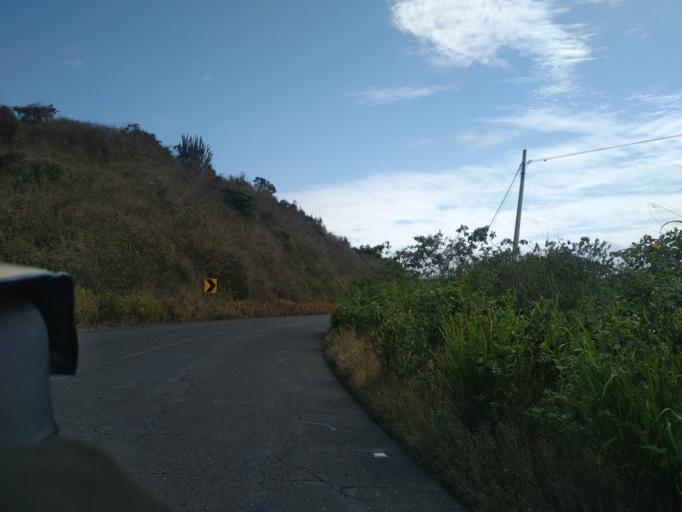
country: EC
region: Manabi
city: Jipijapa
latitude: -1.4455
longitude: -80.7558
